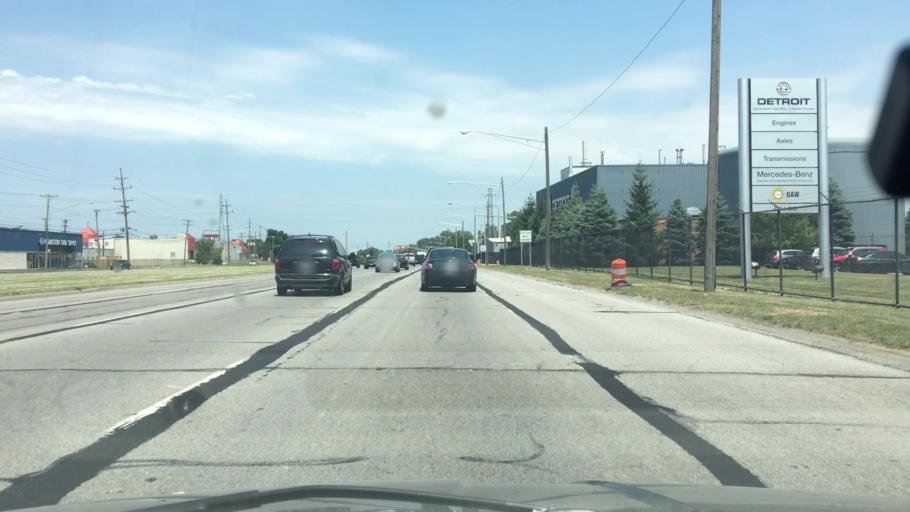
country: US
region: Michigan
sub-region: Wayne County
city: Redford
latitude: 42.3747
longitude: -83.2753
